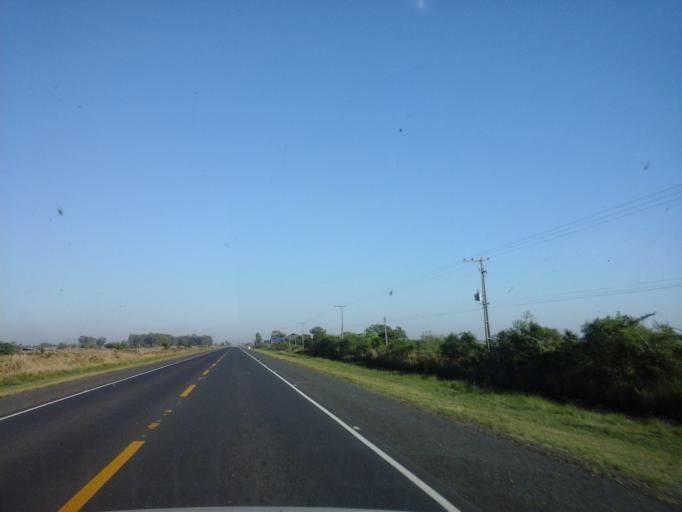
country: PY
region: Neembucu
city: Pilar
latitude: -26.8481
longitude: -58.2393
